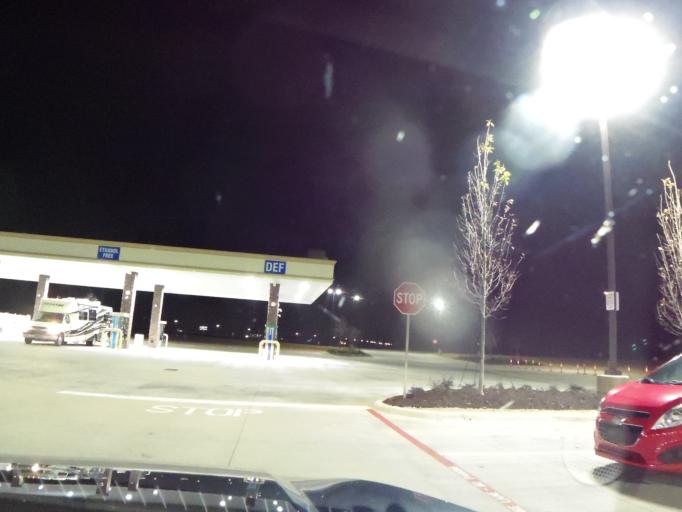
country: US
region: Georgia
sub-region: Houston County
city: Centerville
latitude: 32.5834
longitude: -83.7402
